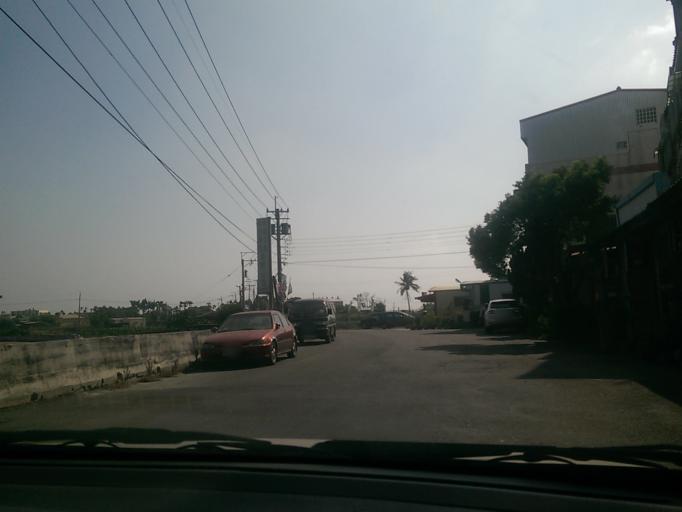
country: TW
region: Taiwan
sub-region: Changhua
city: Chang-hua
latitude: 23.9698
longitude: 120.5103
